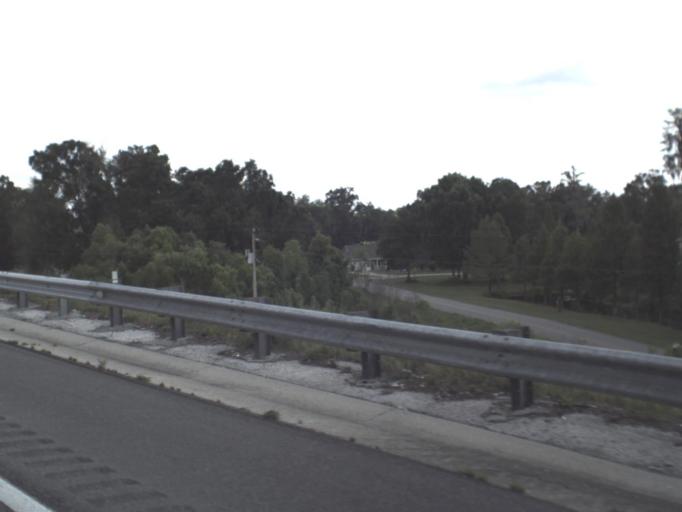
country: US
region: Florida
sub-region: Columbia County
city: Lake City
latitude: 30.1457
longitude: -82.6710
